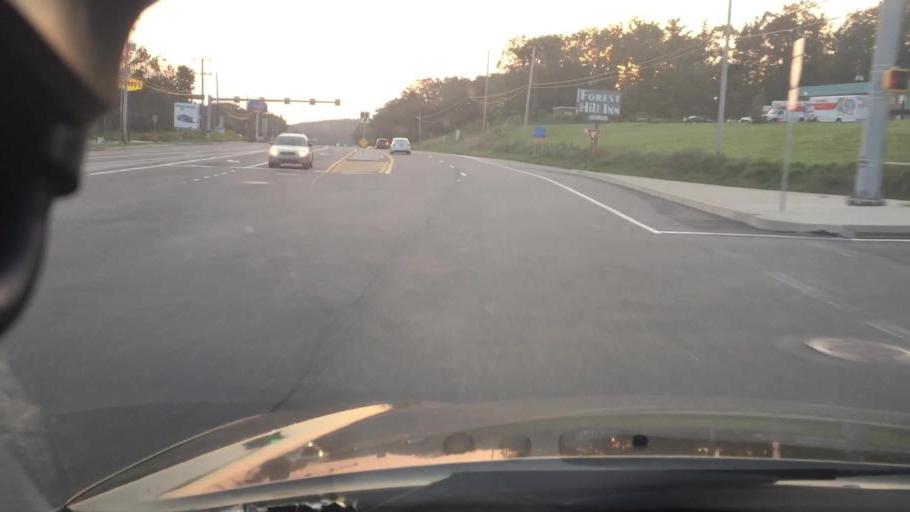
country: US
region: Pennsylvania
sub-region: Luzerne County
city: Conyngham
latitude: 40.9819
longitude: -76.0242
